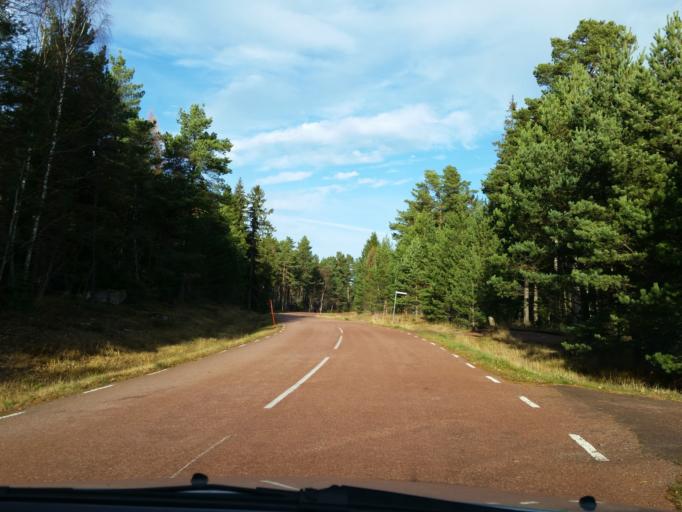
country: AX
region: Alands landsbygd
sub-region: Saltvik
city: Saltvik
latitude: 60.3511
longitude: 20.0954
